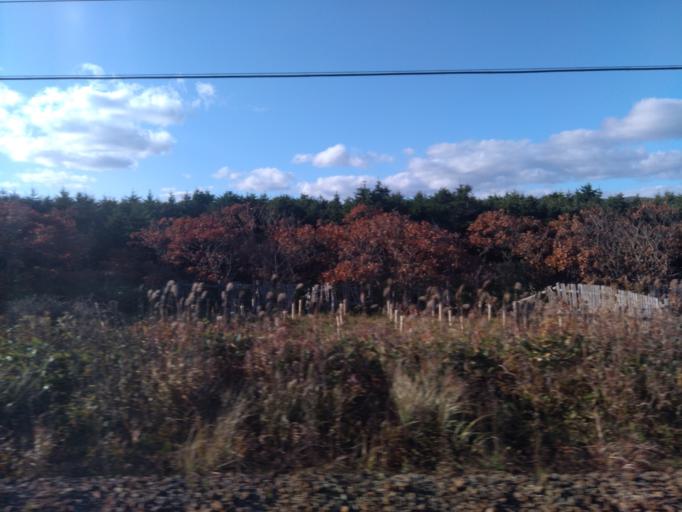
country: JP
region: Hokkaido
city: Niseko Town
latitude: 42.5476
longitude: 140.4142
